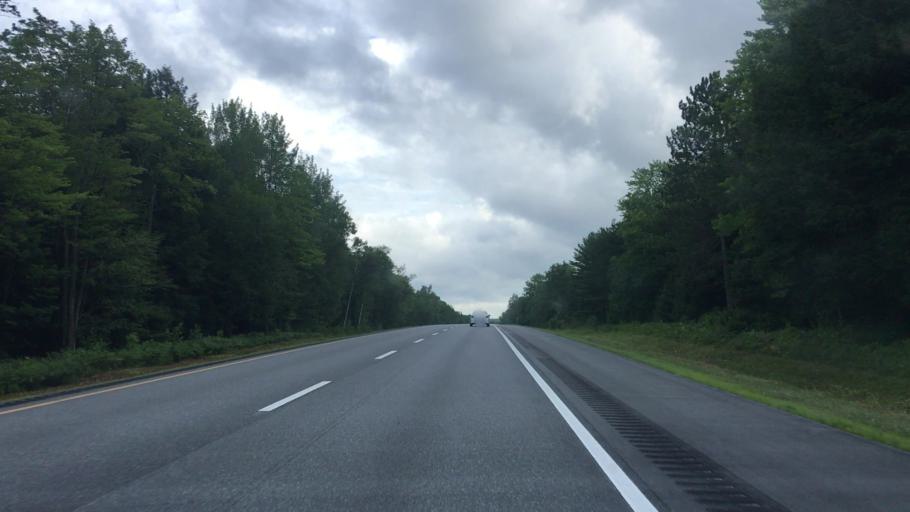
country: US
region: Maine
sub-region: Waldo County
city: Burnham
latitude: 44.7207
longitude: -69.4437
